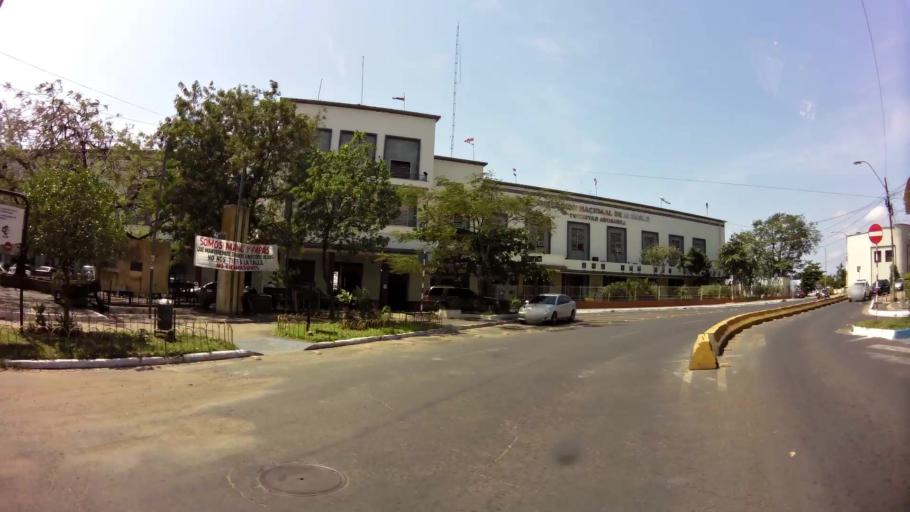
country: PY
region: Asuncion
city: Asuncion
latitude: -25.2767
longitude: -57.6401
